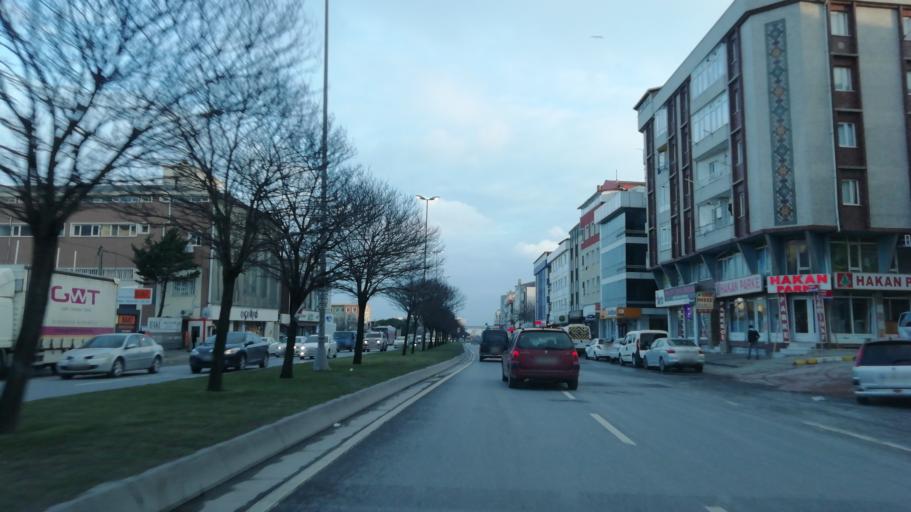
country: TR
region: Istanbul
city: Yakuplu
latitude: 41.0042
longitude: 28.7082
